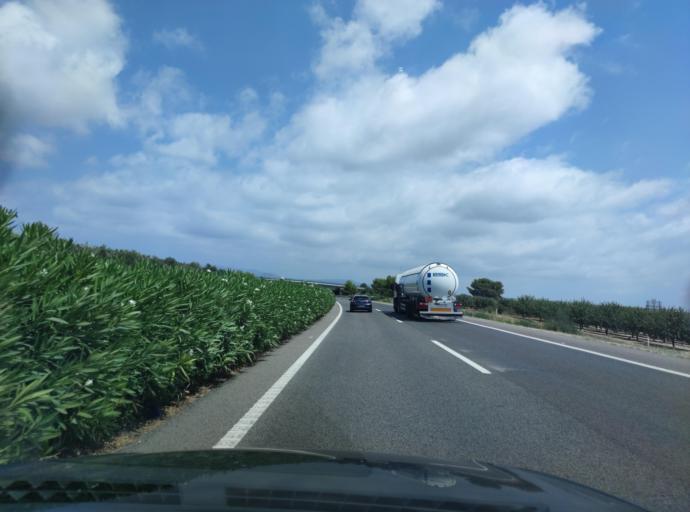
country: ES
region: Catalonia
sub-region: Provincia de Tarragona
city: Amposta
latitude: 40.7375
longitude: 0.5908
